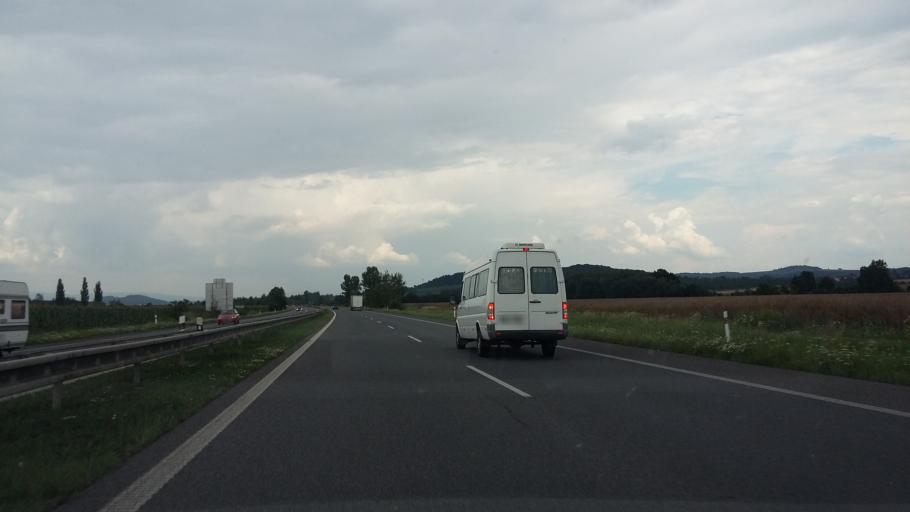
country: CZ
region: Central Bohemia
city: Bakov nad Jizerou
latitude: 50.4890
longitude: 14.9710
